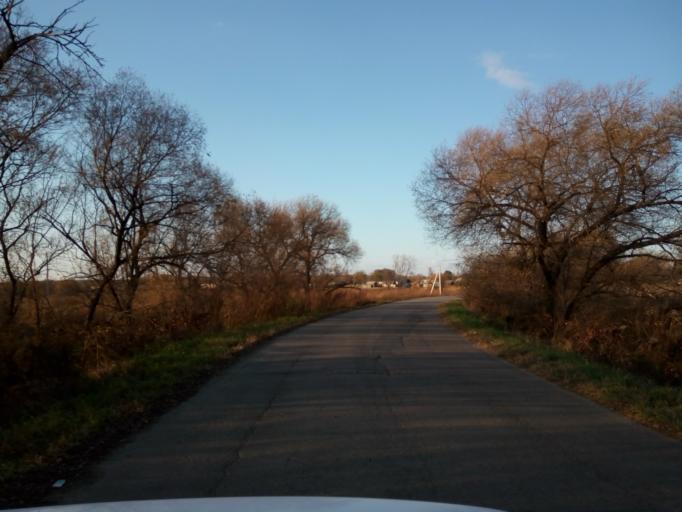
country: RU
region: Primorskiy
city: Lazo
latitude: 45.8248
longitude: 133.6128
